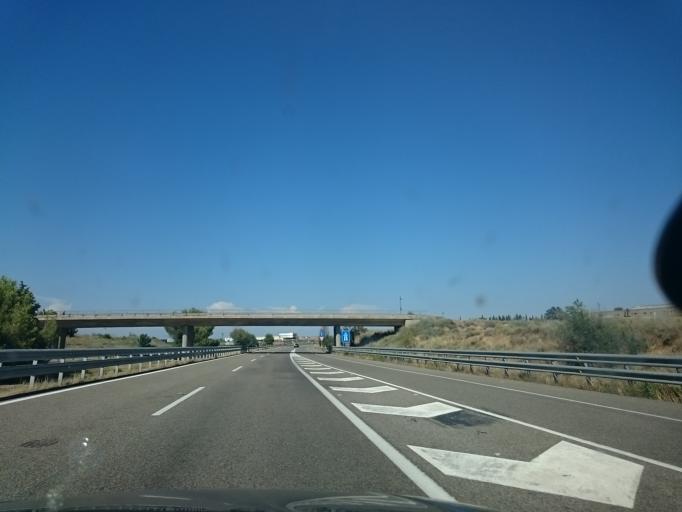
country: ES
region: Catalonia
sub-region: Provincia de Lleida
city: Soses
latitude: 41.5380
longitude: 0.4784
